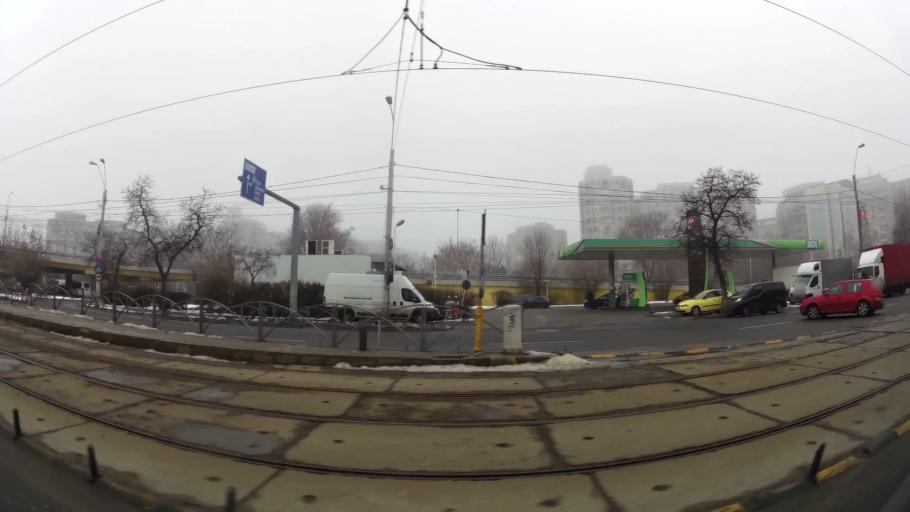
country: RO
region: Ilfov
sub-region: Comuna Chiajna
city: Rosu
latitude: 44.4550
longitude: 26.0566
